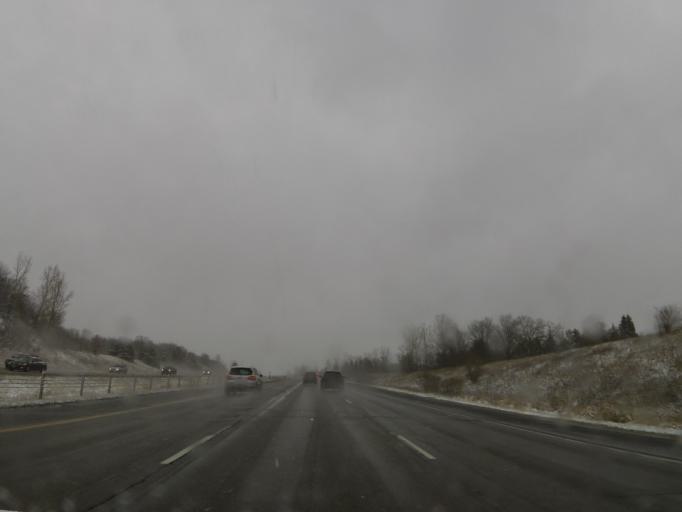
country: US
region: Minnesota
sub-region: Dakota County
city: Inver Grove Heights
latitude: 44.8631
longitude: -93.0911
